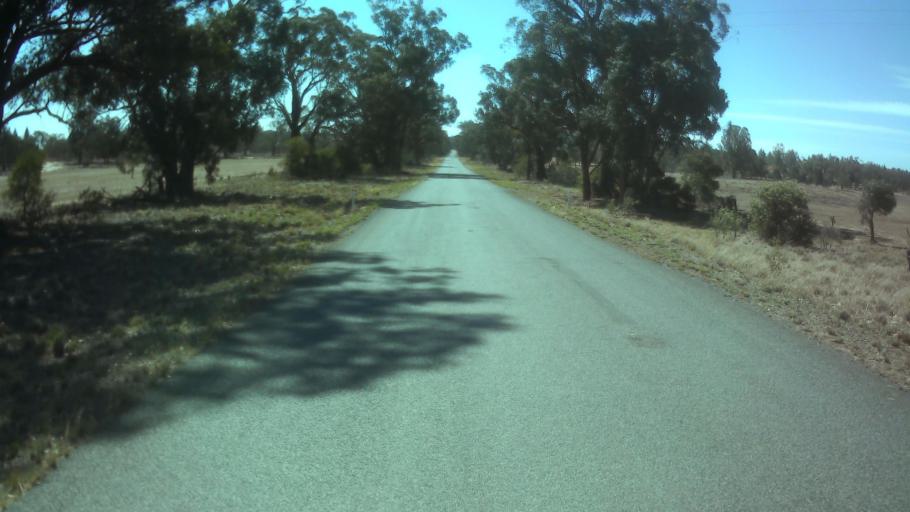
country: AU
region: New South Wales
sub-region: Weddin
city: Grenfell
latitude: -33.8038
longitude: 147.8957
